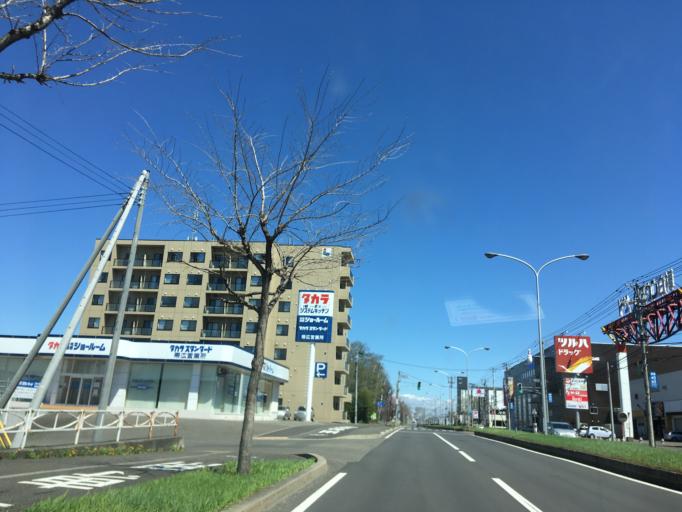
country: JP
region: Hokkaido
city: Obihiro
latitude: 42.9198
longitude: 143.1724
